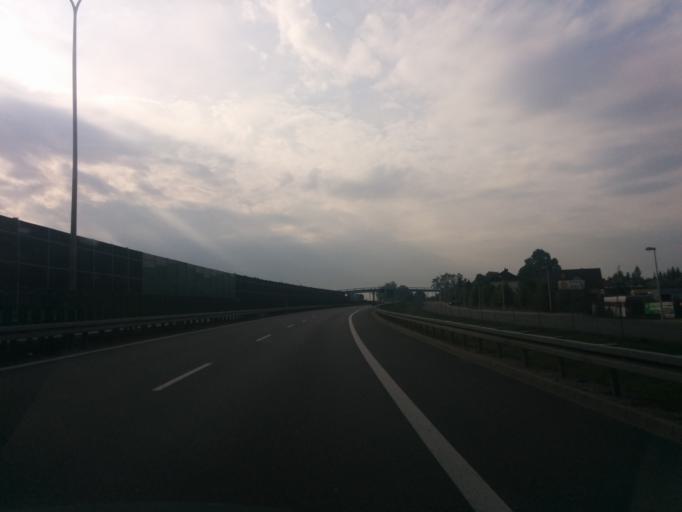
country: PL
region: Masovian Voivodeship
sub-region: Powiat bialobrzeski
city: Stara Blotnica
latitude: 51.5649
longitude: 21.0259
